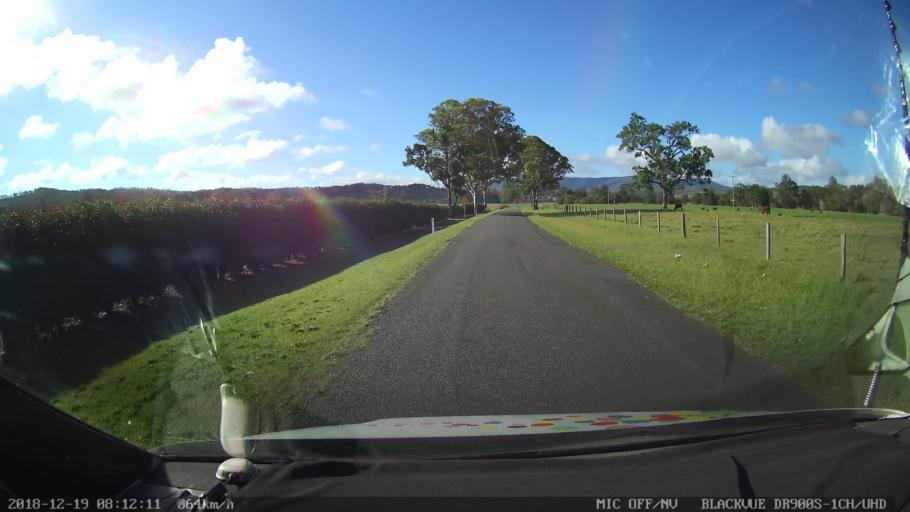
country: AU
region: Queensland
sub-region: Logan
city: Cedar Vale
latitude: -28.2251
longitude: 152.8920
